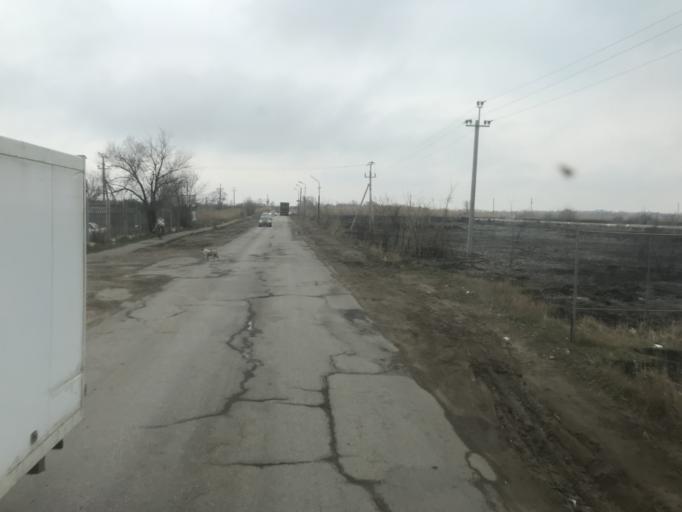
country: RU
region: Volgograd
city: Svetlyy Yar
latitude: 48.5268
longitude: 44.6136
